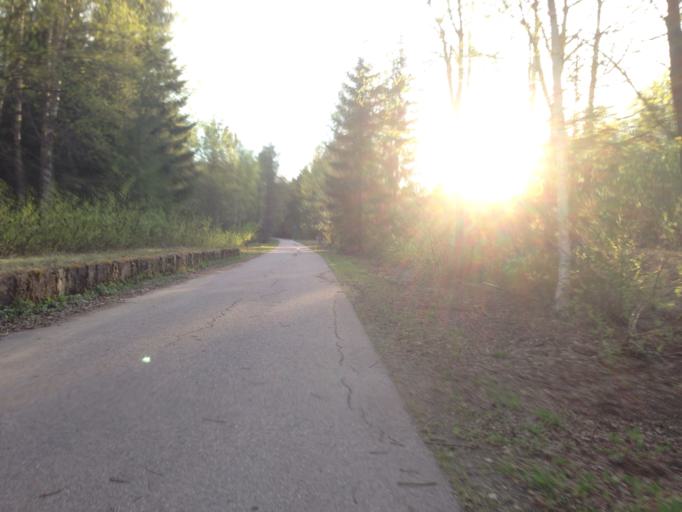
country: SE
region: Dalarna
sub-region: Ludvika Kommun
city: Ludvika
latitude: 60.1414
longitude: 15.1023
